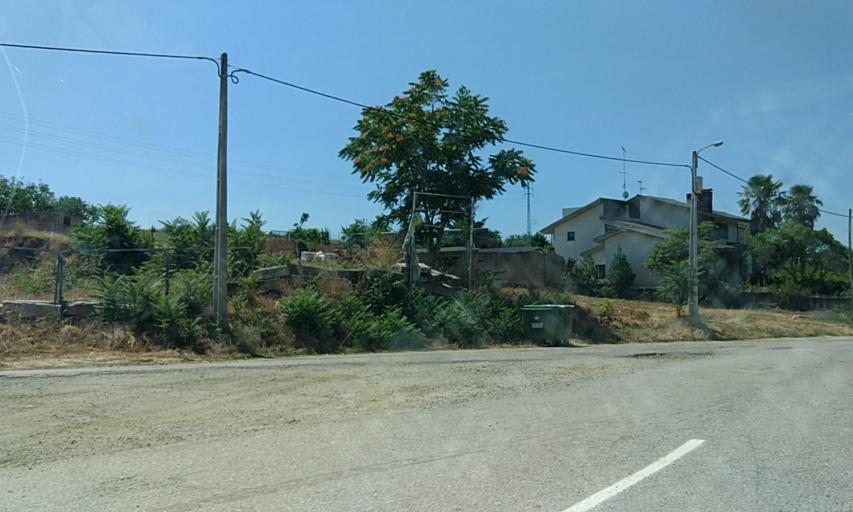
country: PT
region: Braganca
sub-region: Braganca Municipality
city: Braganca
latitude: 41.7790
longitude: -6.7821
